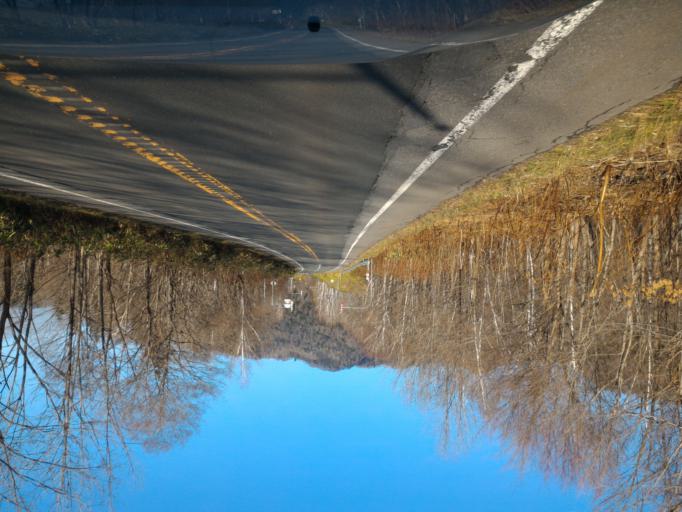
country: JP
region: Hokkaido
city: Ashibetsu
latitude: 43.2989
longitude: 142.1126
